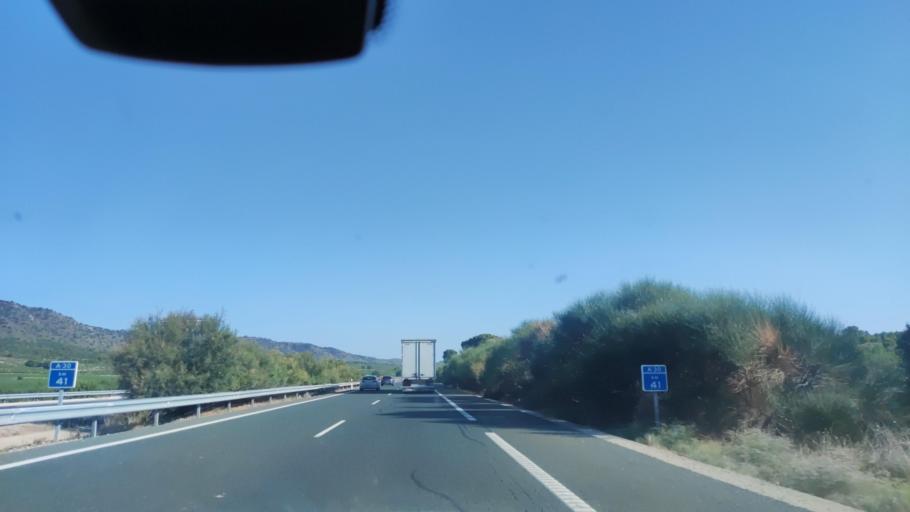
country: ES
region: Castille-La Mancha
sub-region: Provincia de Albacete
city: Tobarra
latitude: 38.6639
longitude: -1.6634
